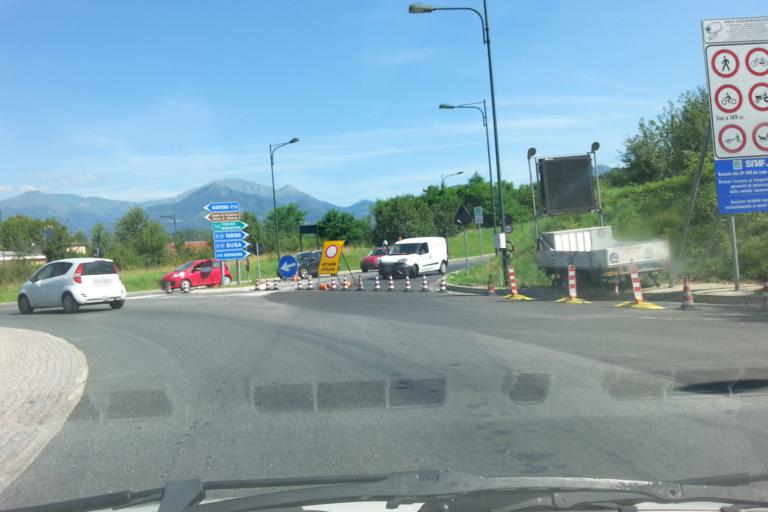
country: IT
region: Piedmont
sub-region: Provincia di Torino
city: Avigliana
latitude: 45.0602
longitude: 7.3928
